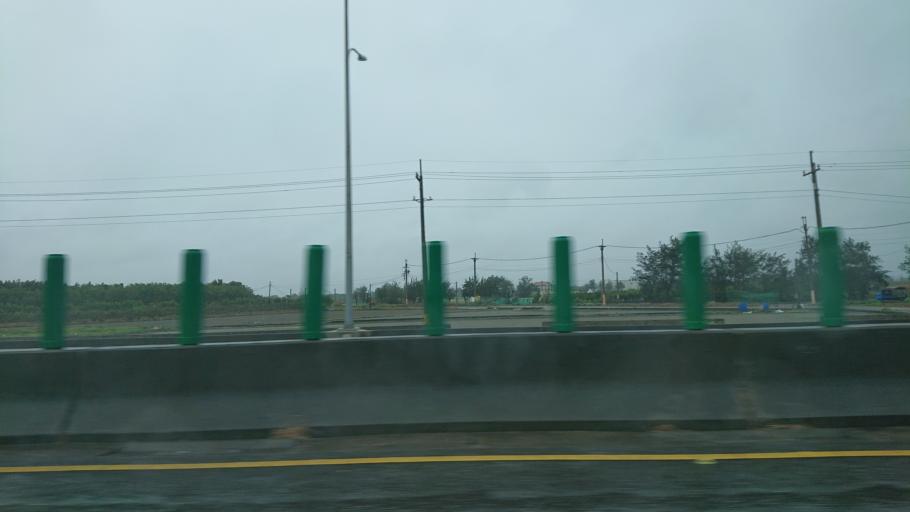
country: TW
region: Taiwan
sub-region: Chiayi
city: Taibao
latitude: 23.7277
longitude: 120.2205
